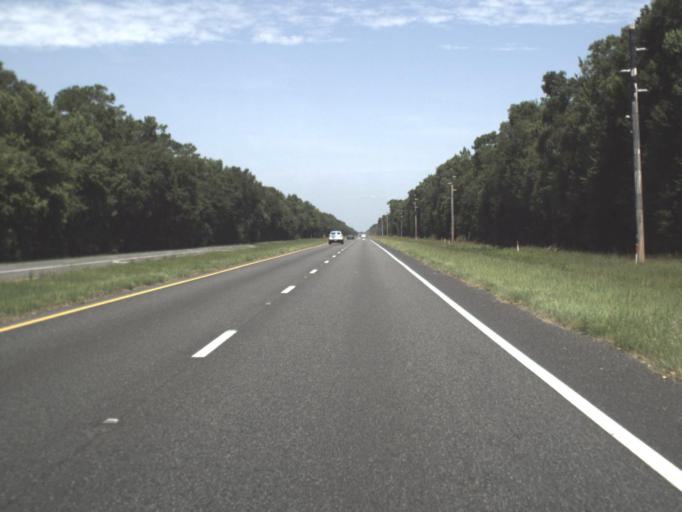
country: US
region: Florida
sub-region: Dixie County
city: Cross City
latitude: 29.6595
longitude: -83.1933
